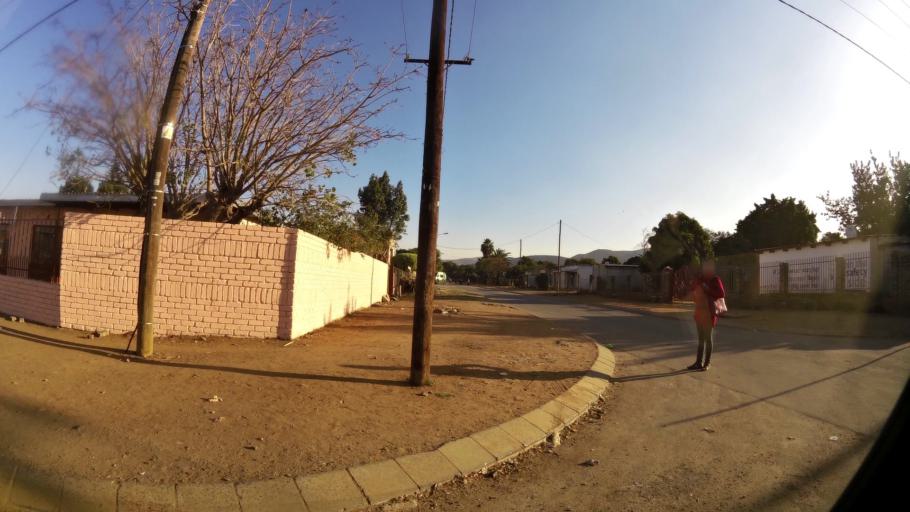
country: ZA
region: North-West
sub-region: Bojanala Platinum District Municipality
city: Rustenburg
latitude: -25.6432
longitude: 27.2239
